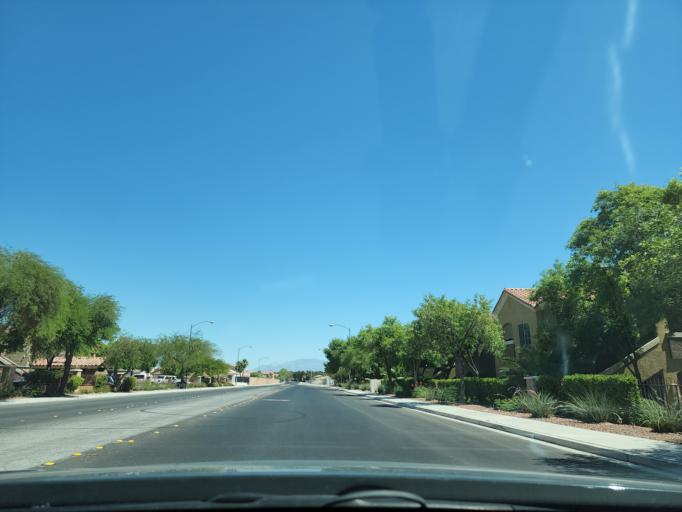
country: US
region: Nevada
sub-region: Clark County
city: Spring Valley
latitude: 36.0857
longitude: -115.2519
